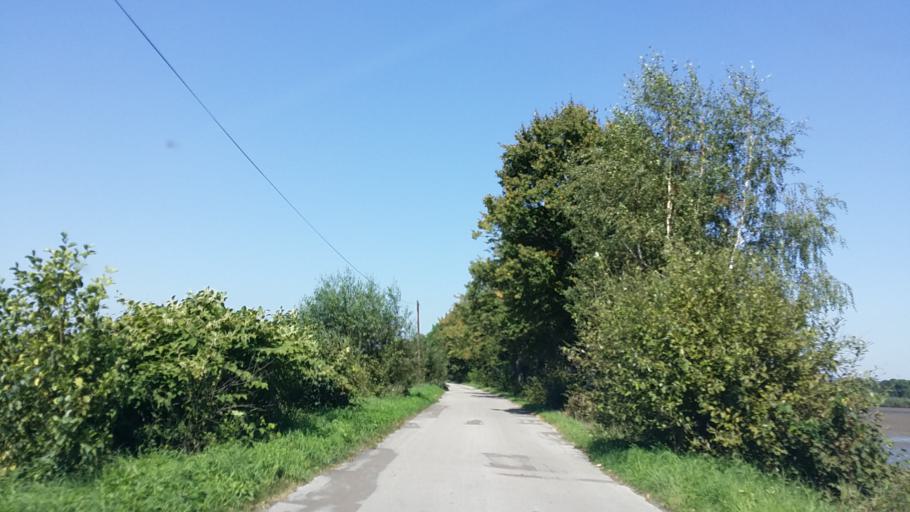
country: PL
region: Lesser Poland Voivodeship
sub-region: Powiat oswiecimski
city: Przeciszow
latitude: 50.0092
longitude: 19.4047
